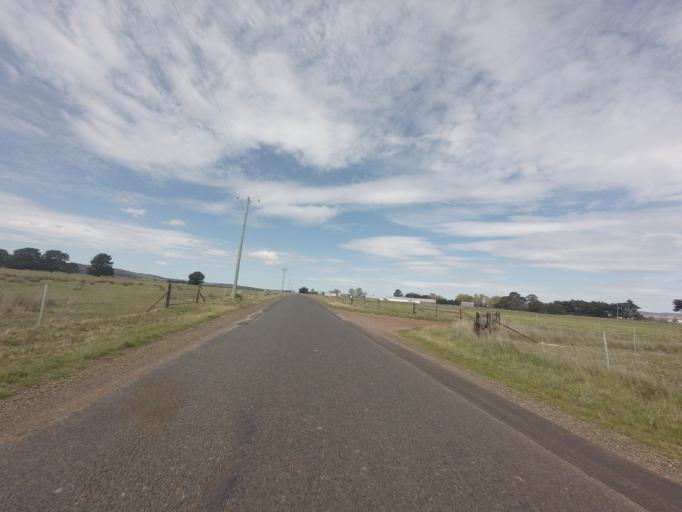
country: AU
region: Tasmania
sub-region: Northern Midlands
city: Evandale
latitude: -41.8102
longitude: 147.2857
